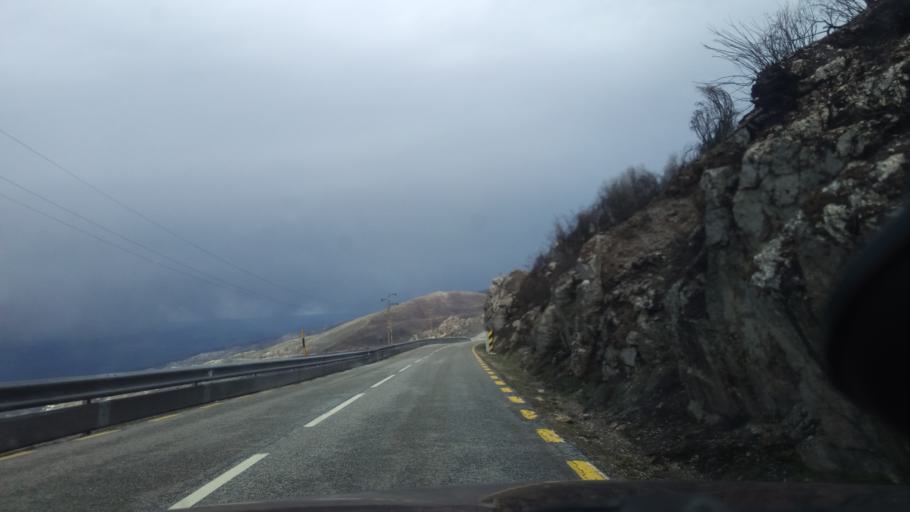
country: PT
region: Guarda
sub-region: Manteigas
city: Manteigas
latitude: 40.4251
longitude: -7.6148
